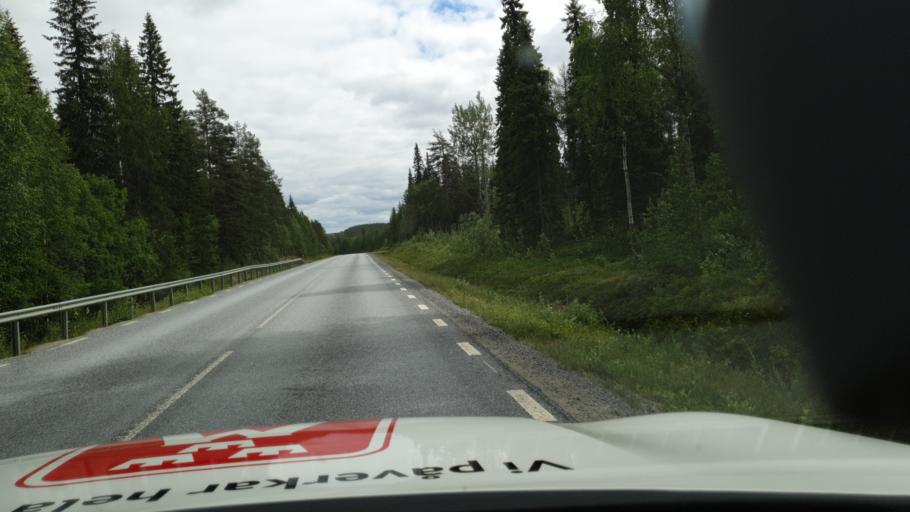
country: SE
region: Vaesterbotten
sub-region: Lycksele Kommun
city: Lycksele
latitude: 64.0304
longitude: 18.6305
